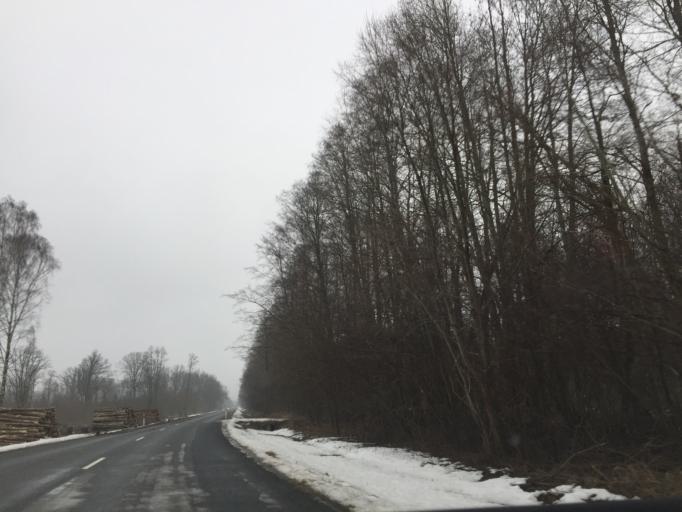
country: EE
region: Saare
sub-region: Kuressaare linn
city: Kuressaare
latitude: 58.3456
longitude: 22.7926
